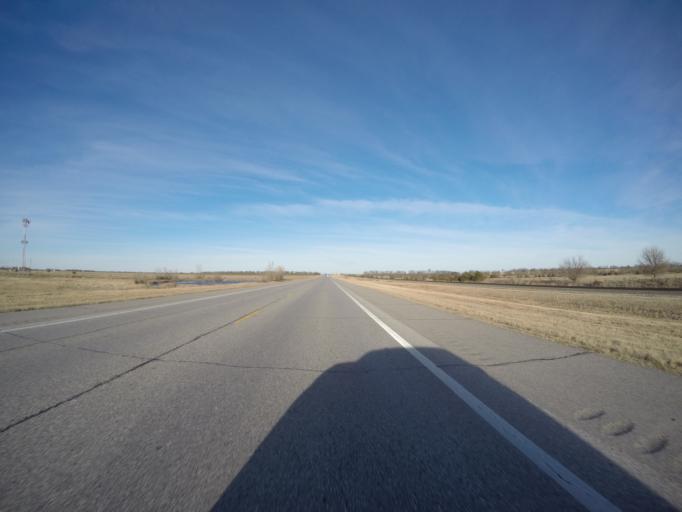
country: US
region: Kansas
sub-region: Harvey County
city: North Newton
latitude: 38.1289
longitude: -97.2435
